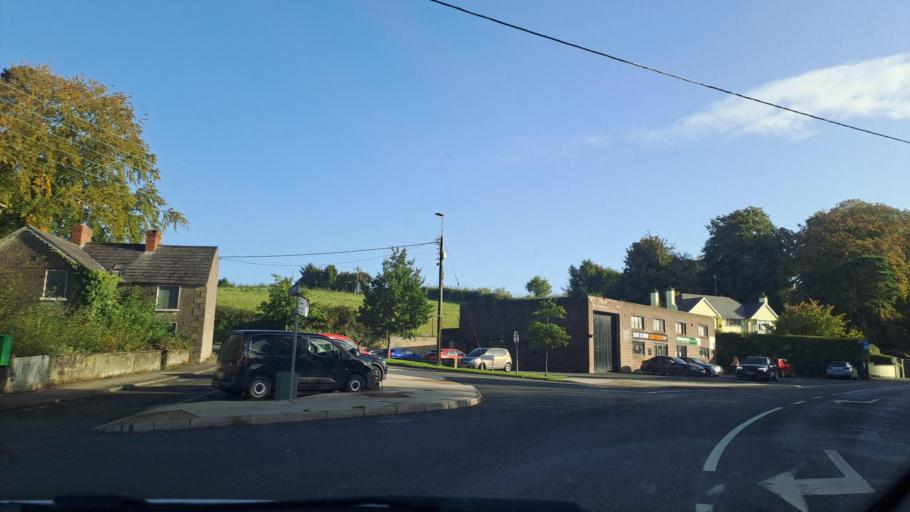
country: IE
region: Ulster
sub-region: County Monaghan
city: Monaghan
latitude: 54.2547
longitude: -6.9649
